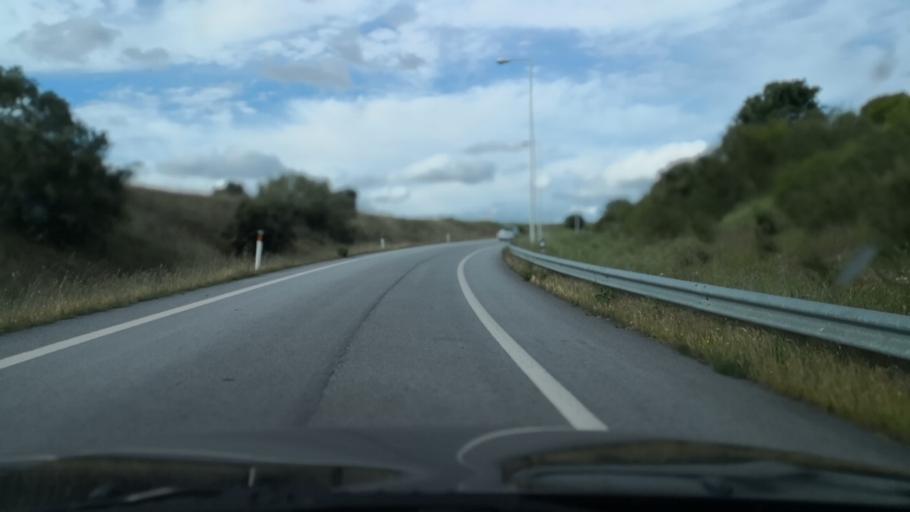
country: PT
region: Evora
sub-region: Evora
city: Evora
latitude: 38.6457
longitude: -7.8562
